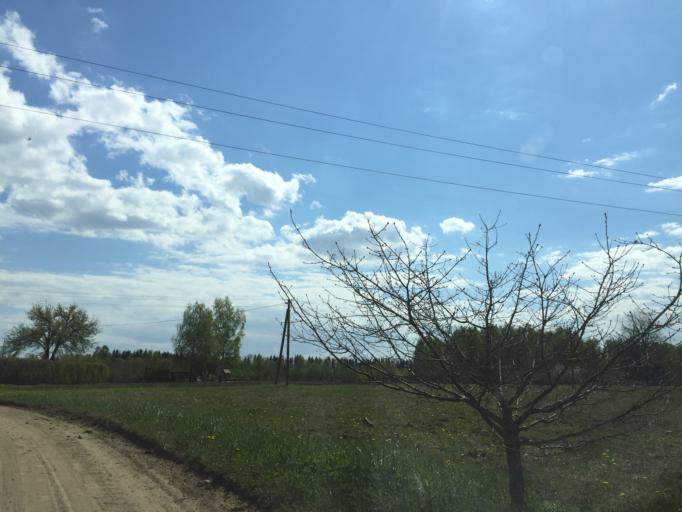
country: LV
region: Saulkrastu
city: Saulkrasti
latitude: 57.3593
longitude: 24.4962
